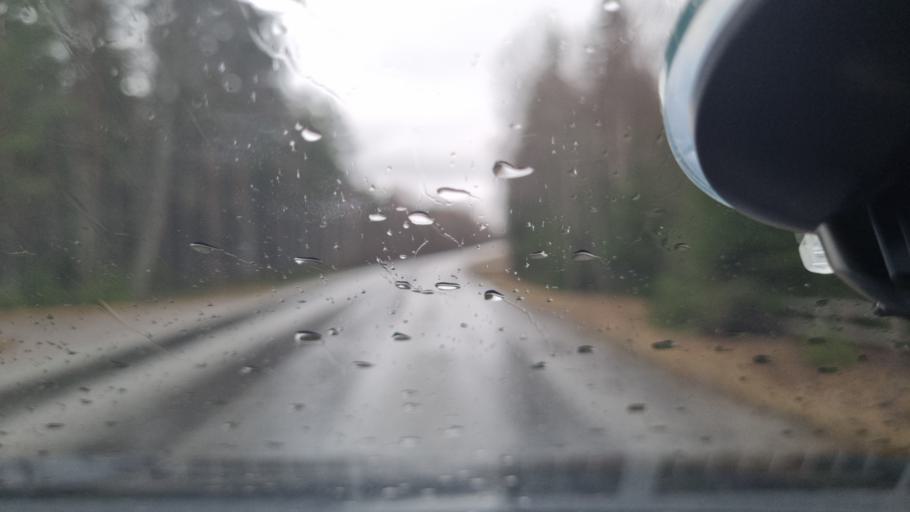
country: SE
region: Stockholm
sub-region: Upplands-Bro Kommun
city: Kungsaengen
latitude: 59.5400
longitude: 17.7412
